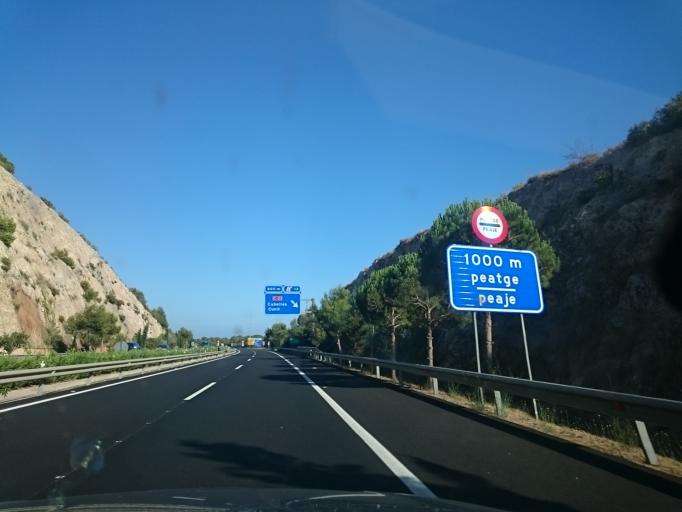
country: ES
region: Catalonia
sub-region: Provincia de Tarragona
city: Cunit
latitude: 41.2113
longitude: 1.6401
